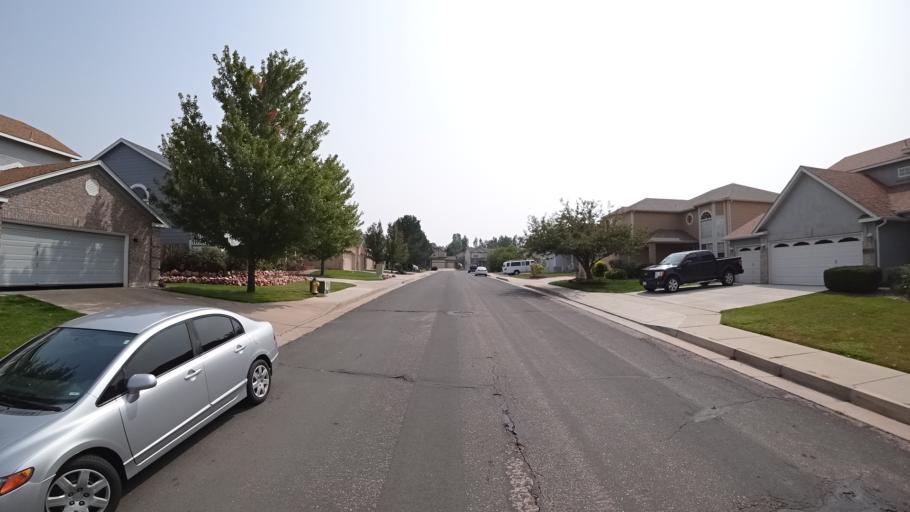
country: US
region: Colorado
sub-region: El Paso County
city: Cimarron Hills
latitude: 38.9183
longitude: -104.7483
